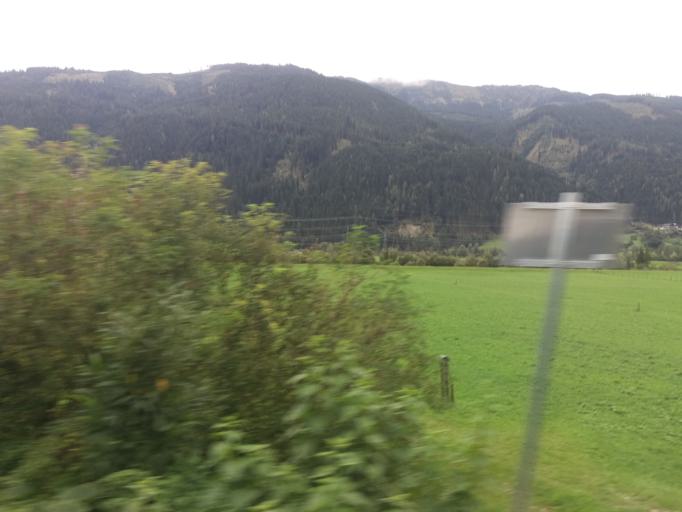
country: AT
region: Salzburg
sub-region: Politischer Bezirk Zell am See
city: Stuhlfelden
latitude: 47.2850
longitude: 12.5320
